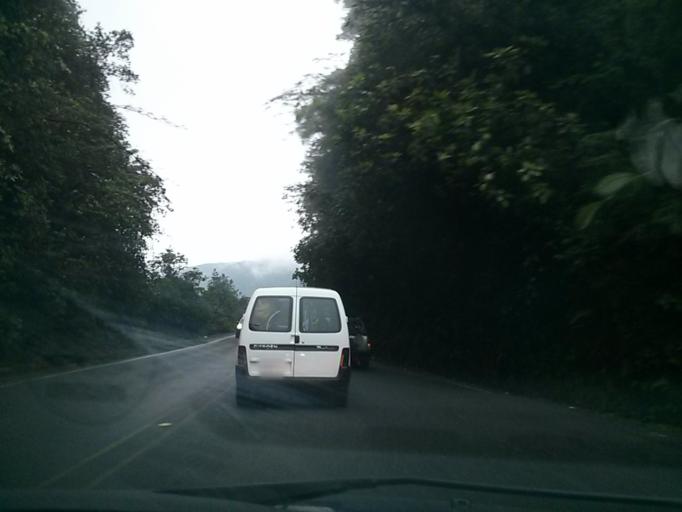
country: CR
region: San Jose
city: Dulce Nombre de Jesus
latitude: 10.0715
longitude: -83.9837
